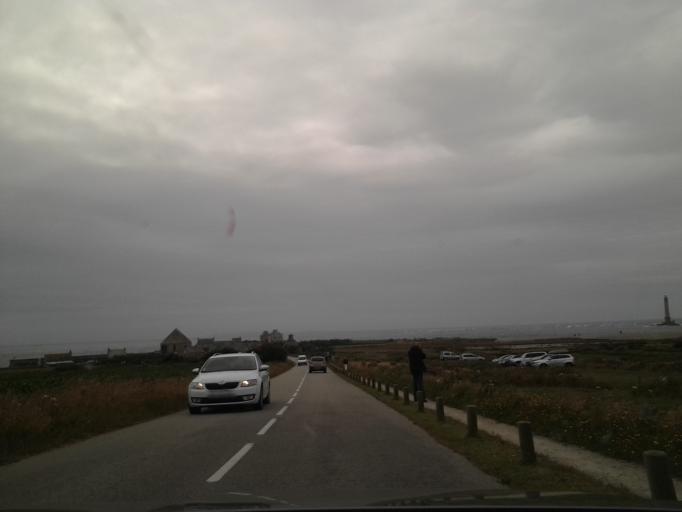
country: FR
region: Lower Normandy
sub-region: Departement de la Manche
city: Beaumont-Hague
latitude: 49.7158
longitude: -1.9394
